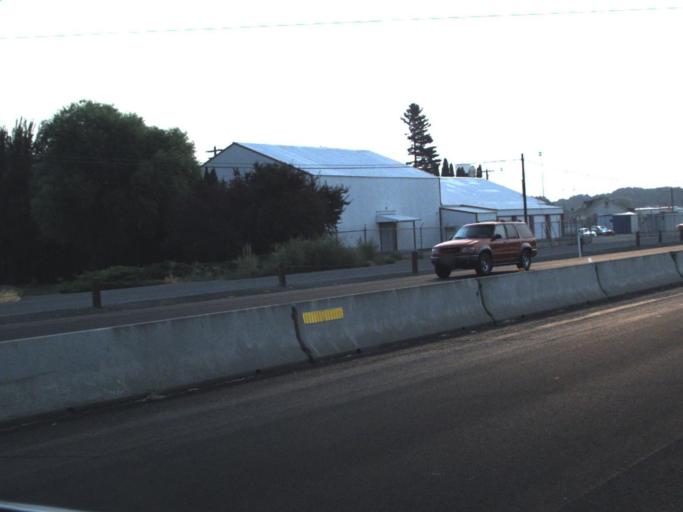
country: US
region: Washington
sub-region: Yakima County
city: Toppenish
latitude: 46.3794
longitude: -120.3384
